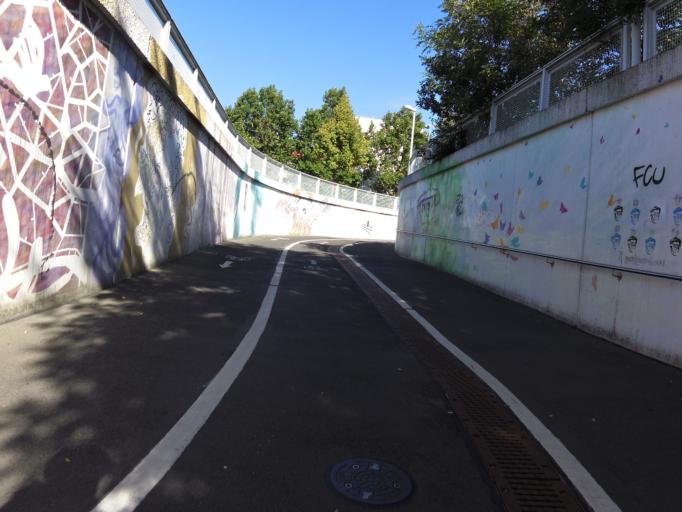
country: DE
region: Saxony-Anhalt
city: Wittenburg
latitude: 51.8659
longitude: 12.6320
